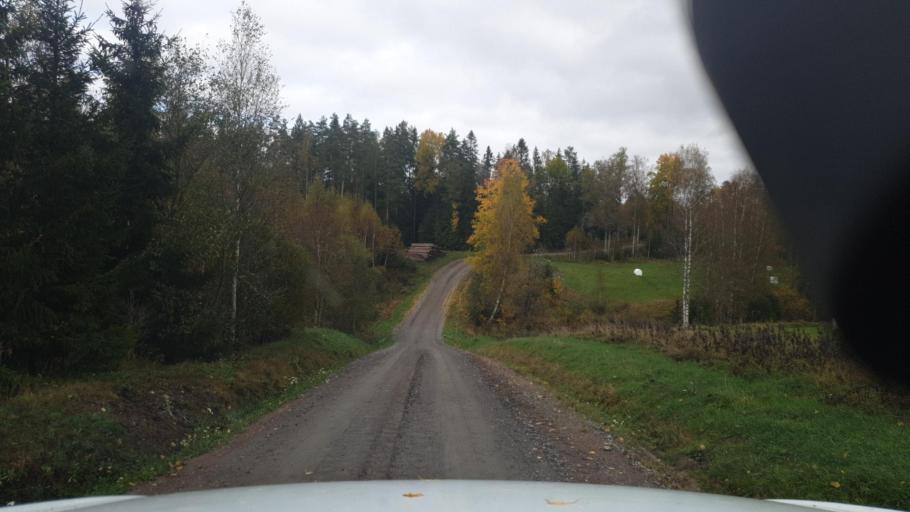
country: SE
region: Vaermland
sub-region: Karlstads Kommun
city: Edsvalla
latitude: 59.4727
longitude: 13.1271
